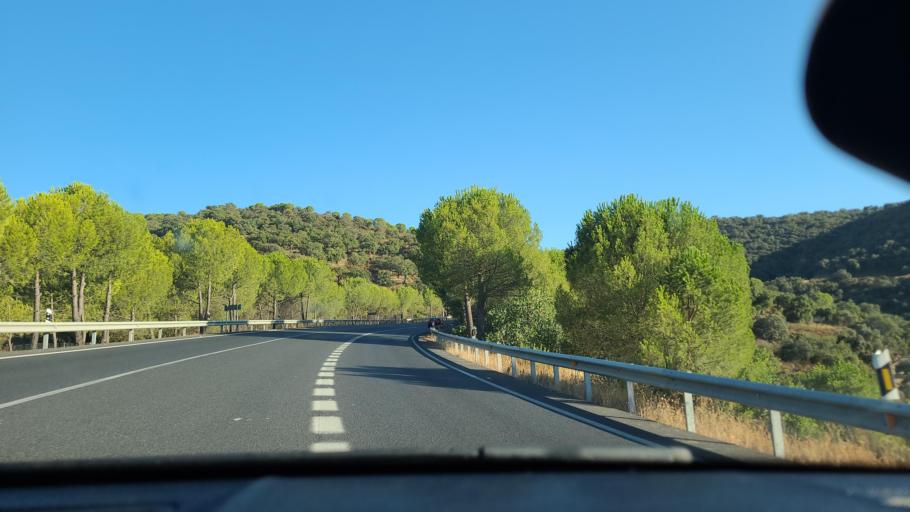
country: ES
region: Andalusia
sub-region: Province of Cordoba
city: Villaharta
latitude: 38.1188
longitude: -4.8888
